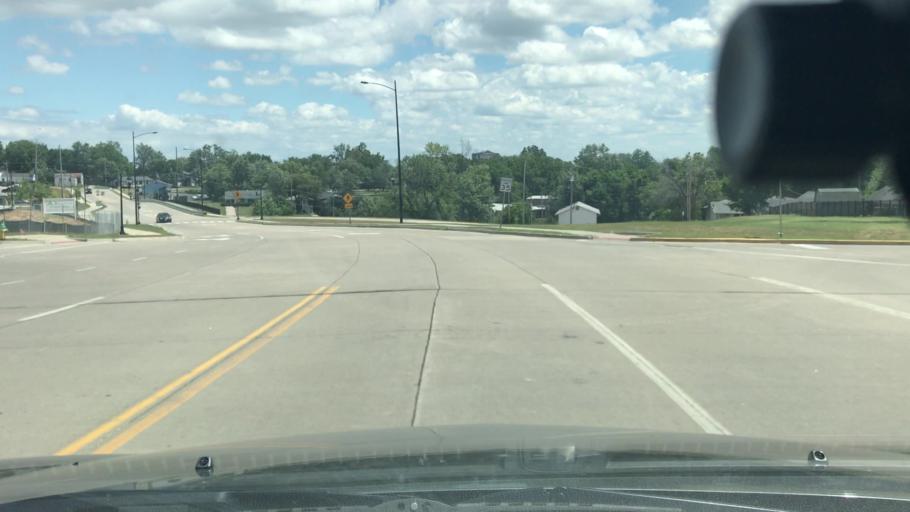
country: US
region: Missouri
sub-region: Saint Charles County
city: Saint Charles
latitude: 38.7819
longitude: -90.5044
